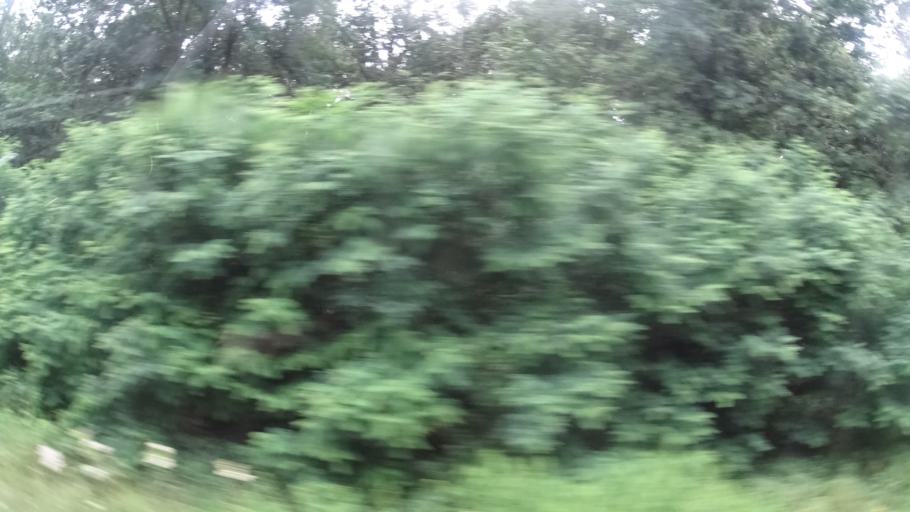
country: DE
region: Rheinland-Pfalz
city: Nanzdietschweiler
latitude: 49.4160
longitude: 7.4458
